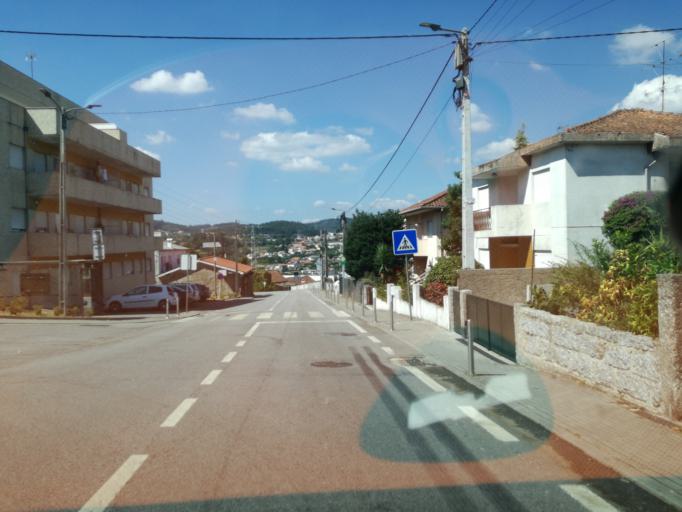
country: PT
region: Braga
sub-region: Guimaraes
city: Guimaraes
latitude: 41.4587
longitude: -8.2835
